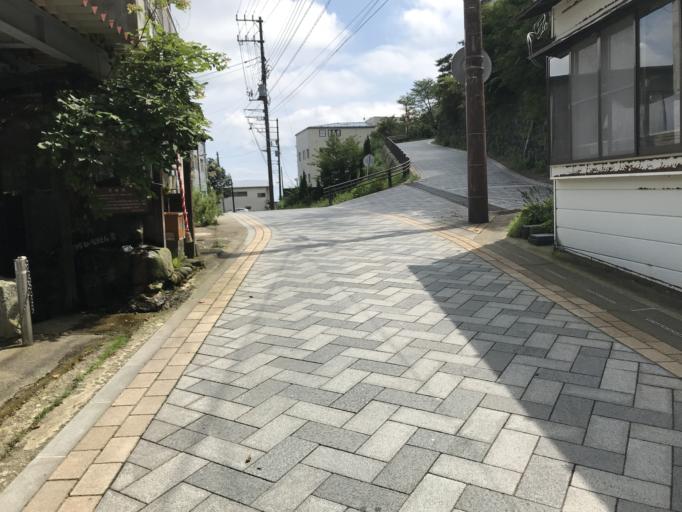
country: JP
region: Tochigi
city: Kuroiso
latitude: 37.0960
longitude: 140.0017
